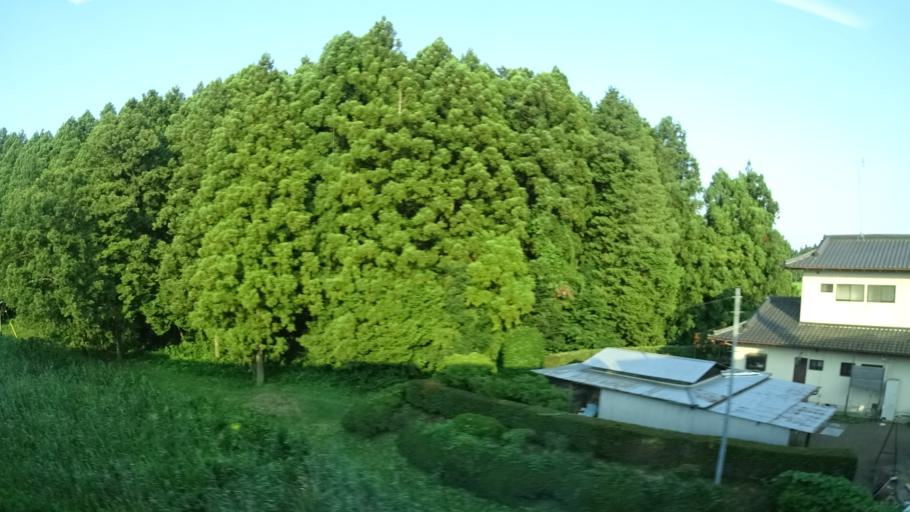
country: JP
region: Ibaraki
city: Tomobe
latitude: 36.3315
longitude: 140.2955
